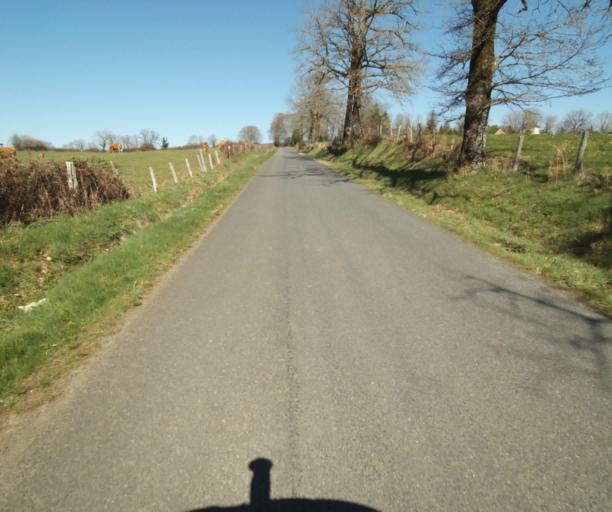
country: FR
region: Limousin
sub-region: Departement de la Correze
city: Saint-Clement
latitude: 45.3335
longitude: 1.6556
